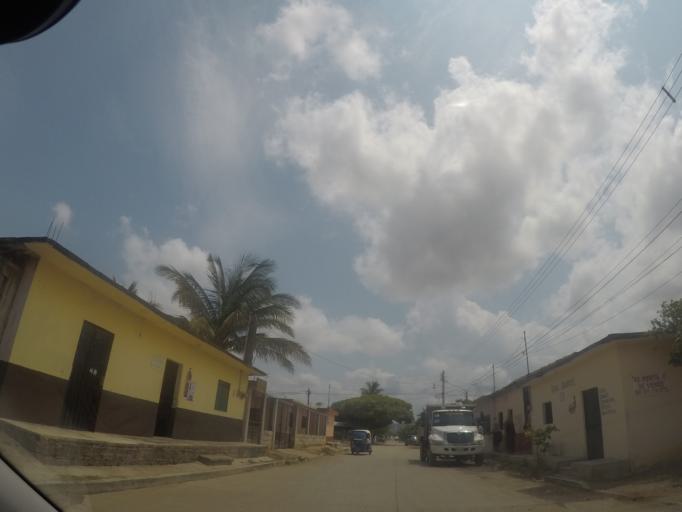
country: MX
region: Oaxaca
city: El Espinal
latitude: 16.5508
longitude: -94.9450
